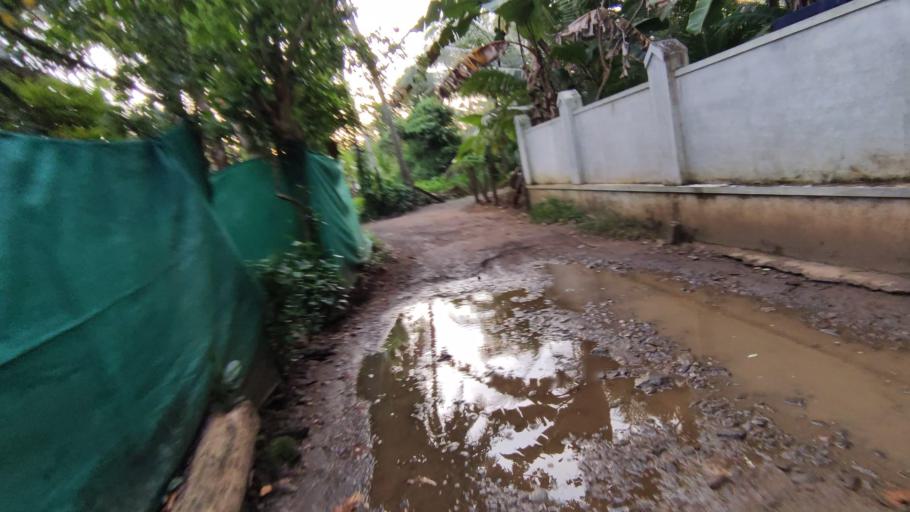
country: IN
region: Kerala
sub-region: Kottayam
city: Kottayam
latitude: 9.5787
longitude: 76.4380
